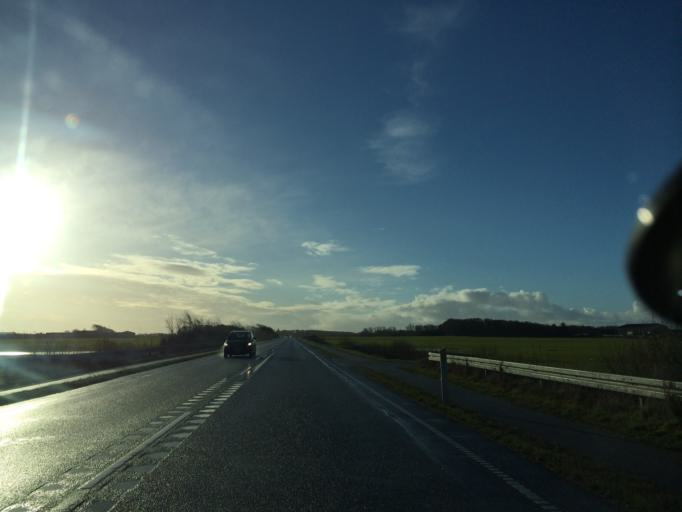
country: DK
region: Central Jutland
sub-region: Ringkobing-Skjern Kommune
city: Ringkobing
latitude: 56.1159
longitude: 8.2698
